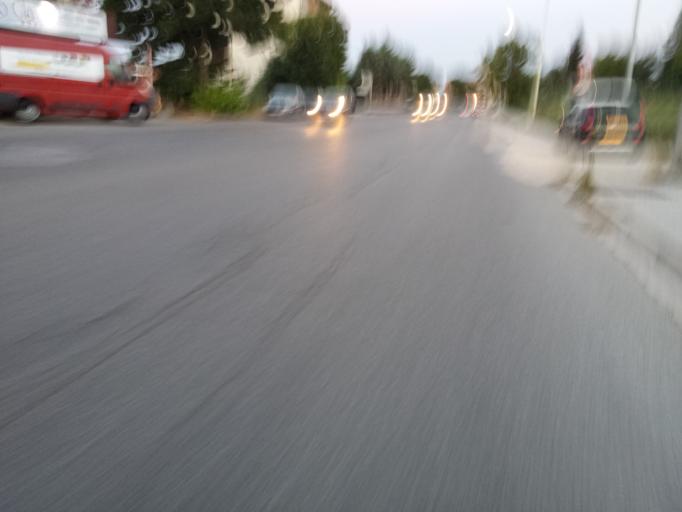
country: IT
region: Molise
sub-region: Provincia di Campobasso
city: Campobasso
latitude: 41.5829
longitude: 14.6735
